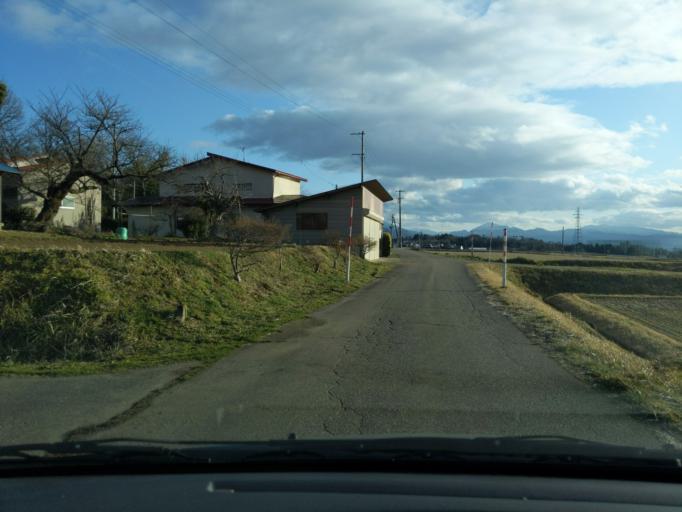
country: JP
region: Fukushima
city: Kitakata
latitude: 37.5479
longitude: 139.9509
